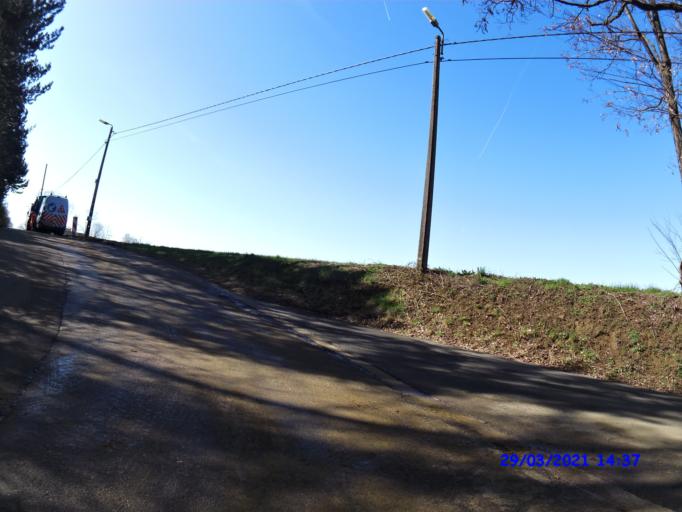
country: BE
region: Flanders
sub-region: Provincie Vlaams-Brabant
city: Glabbeek-Zuurbemde
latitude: 50.9249
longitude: 4.9021
